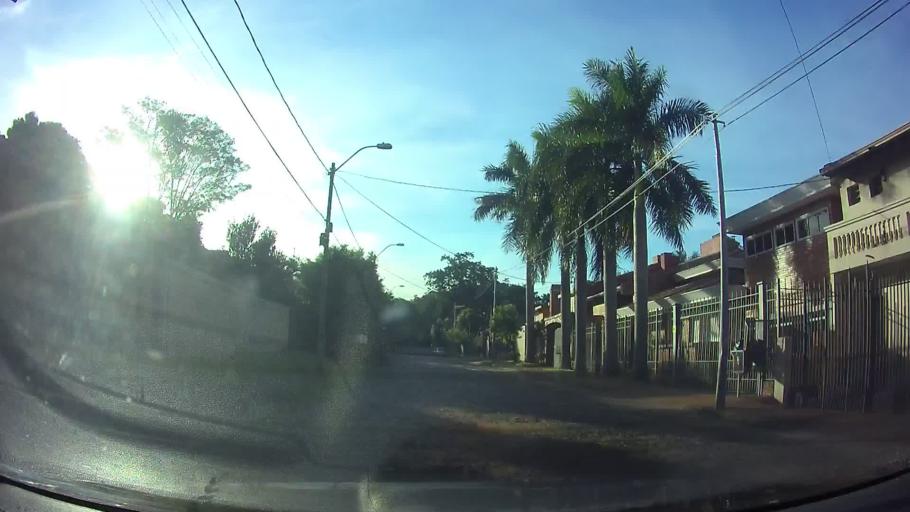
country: PY
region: Asuncion
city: Asuncion
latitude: -25.2741
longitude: -57.5755
